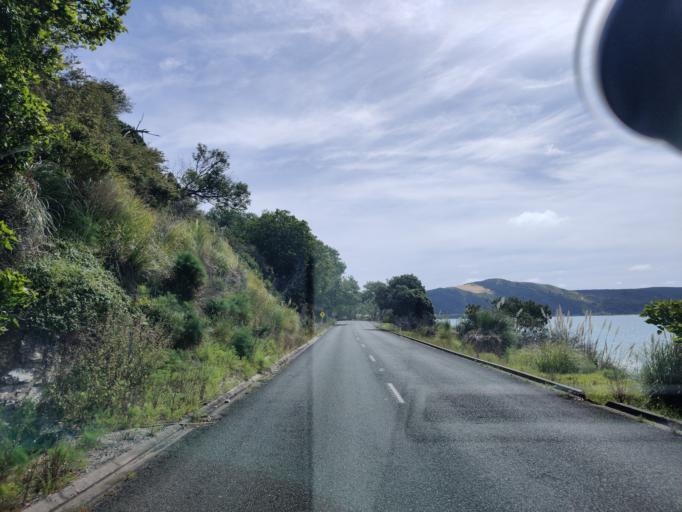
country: NZ
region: Northland
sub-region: Far North District
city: Ahipara
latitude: -35.5031
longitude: 173.3975
